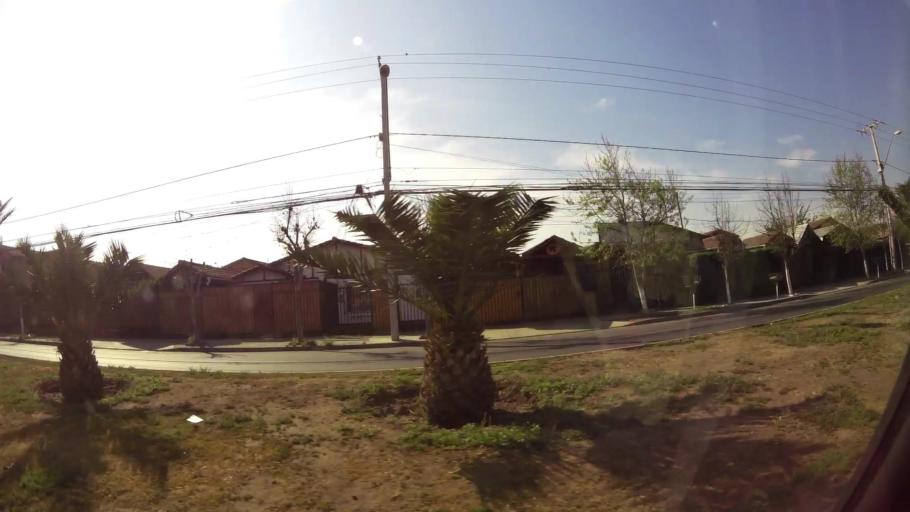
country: CL
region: Santiago Metropolitan
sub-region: Provincia de Santiago
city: Lo Prado
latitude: -33.4552
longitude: -70.7508
